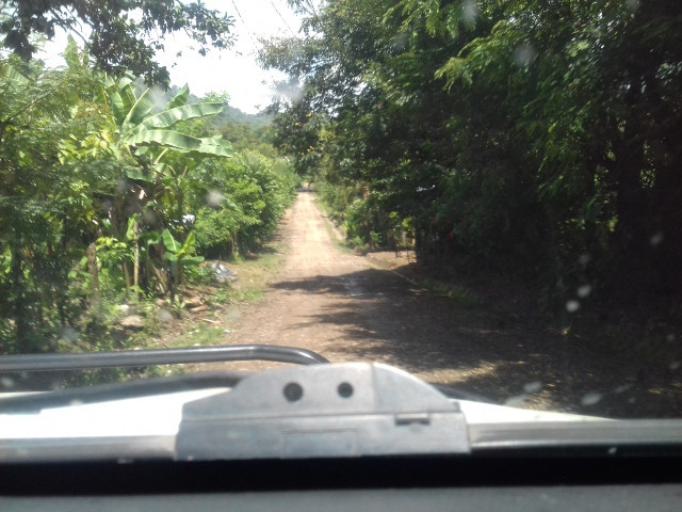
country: NI
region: Matagalpa
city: Rio Blanco
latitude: 12.9732
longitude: -85.3696
